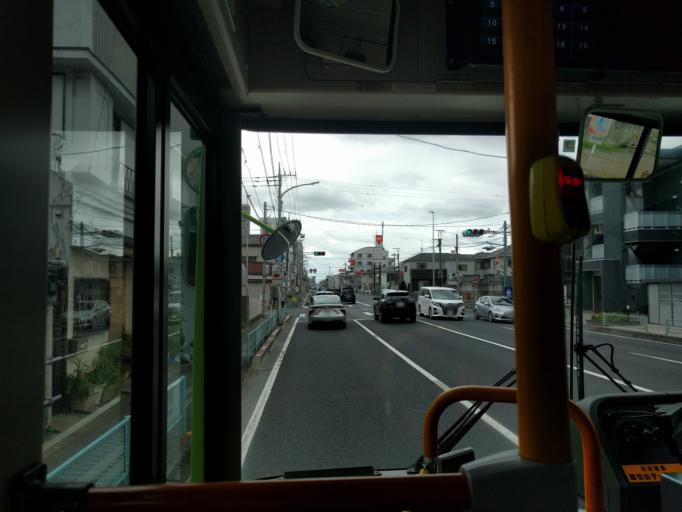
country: JP
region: Saitama
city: Kawaguchi
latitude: 35.8084
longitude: 139.7340
